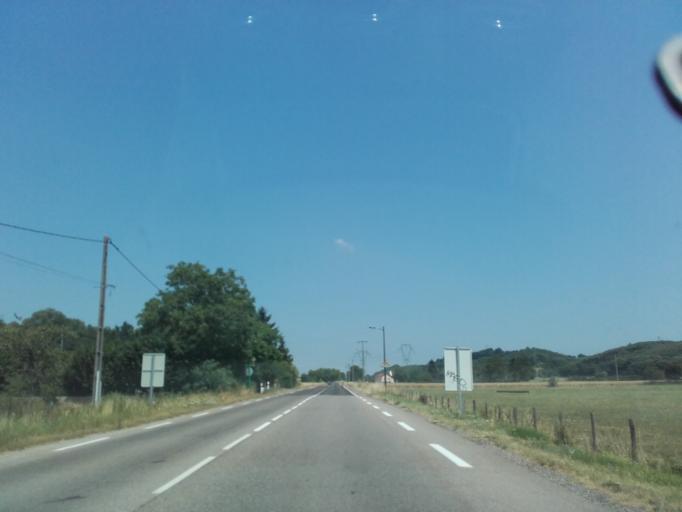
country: FR
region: Rhone-Alpes
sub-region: Departement de l'Isere
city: Champier
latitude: 45.4599
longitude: 5.2922
